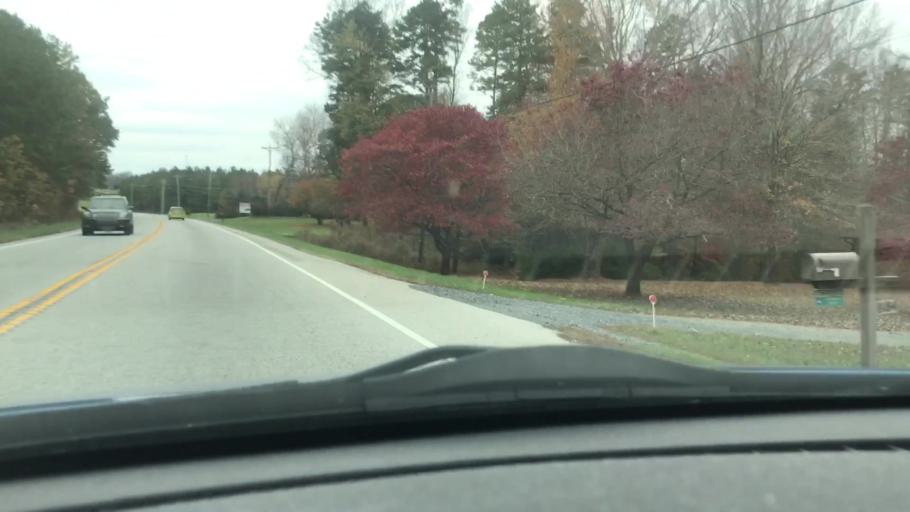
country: US
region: North Carolina
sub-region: Randolph County
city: Trinity
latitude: 35.7495
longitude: -80.0104
